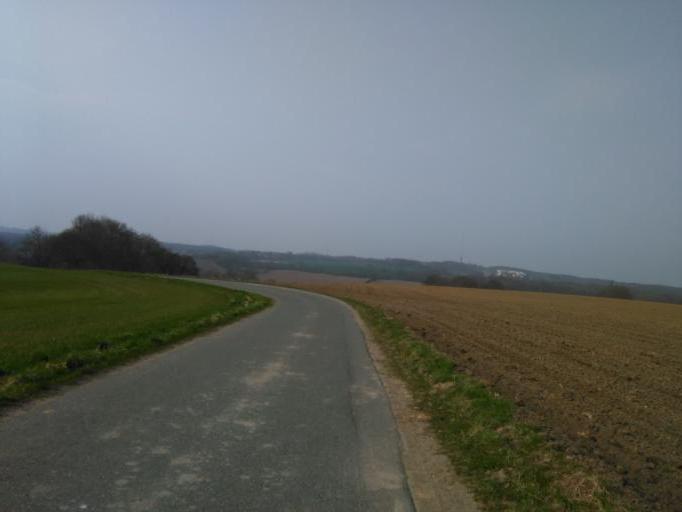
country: DK
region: Central Jutland
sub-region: Arhus Kommune
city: Beder
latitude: 56.0712
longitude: 10.2271
